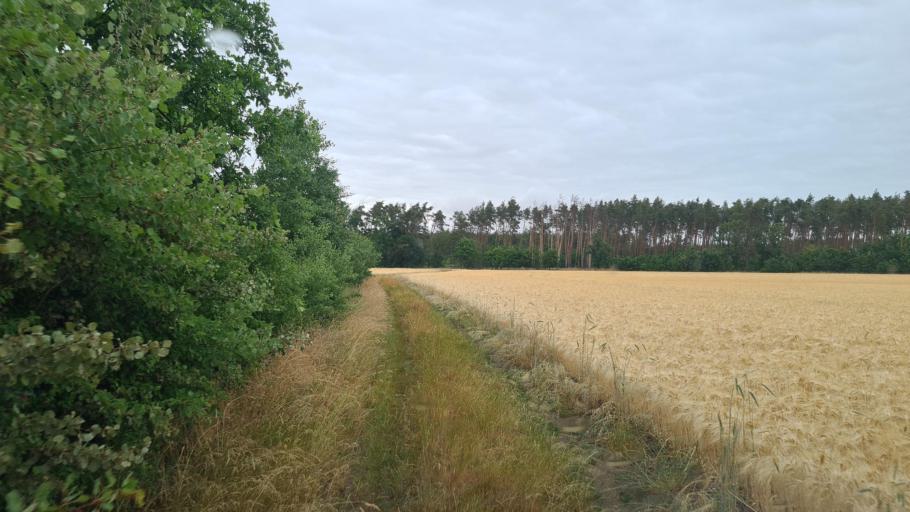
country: DE
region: Brandenburg
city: Bad Liebenwerda
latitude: 51.5007
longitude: 13.3117
